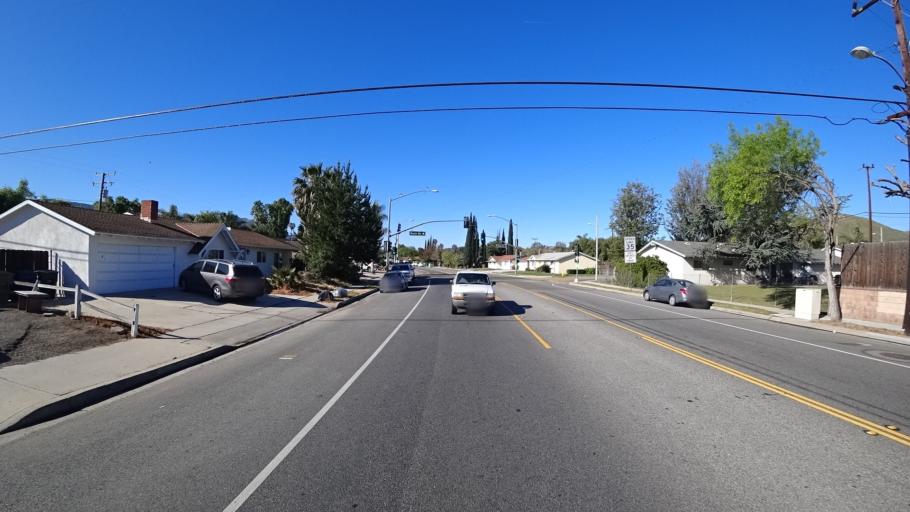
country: US
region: California
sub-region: Ventura County
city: Casa Conejo
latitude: 34.1867
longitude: -118.9439
